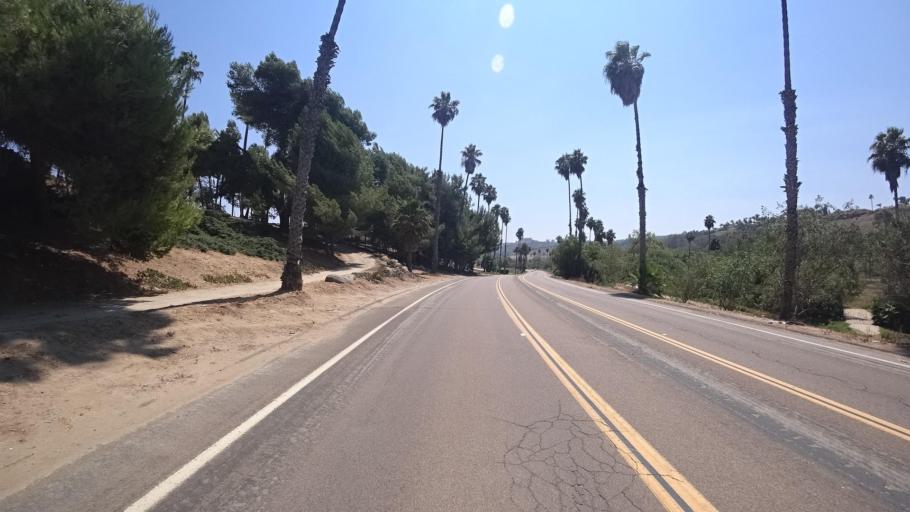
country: US
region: California
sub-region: San Diego County
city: Bonsall
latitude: 33.2886
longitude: -117.2109
